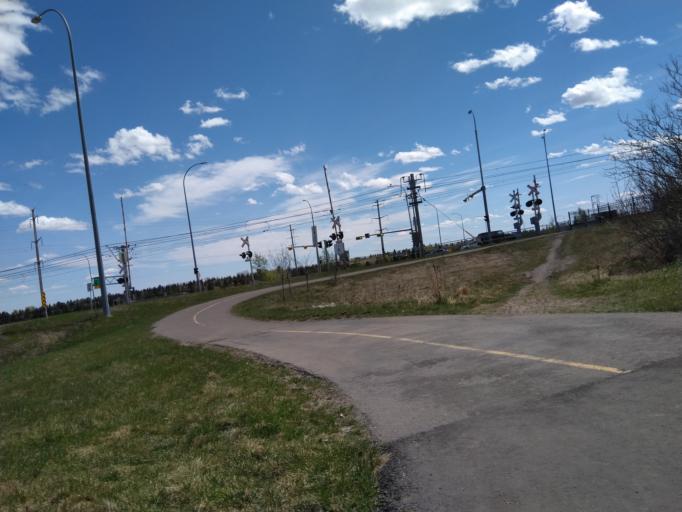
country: CA
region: Alberta
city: Calgary
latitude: 51.0399
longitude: -114.1669
